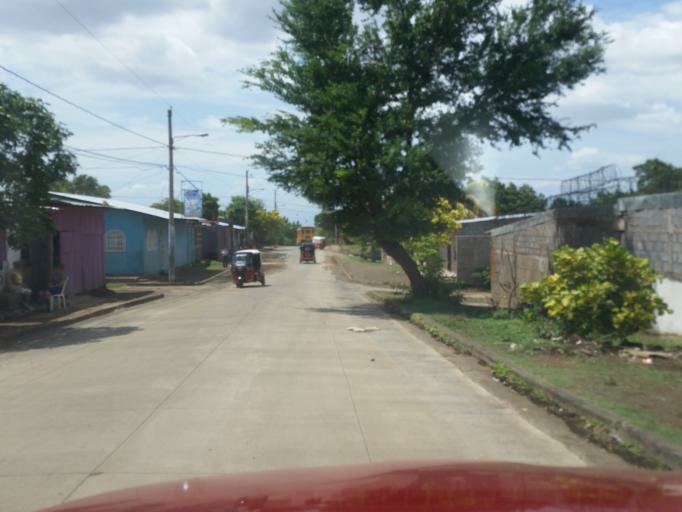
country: NI
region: Managua
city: Managua
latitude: 12.1016
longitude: -86.2273
